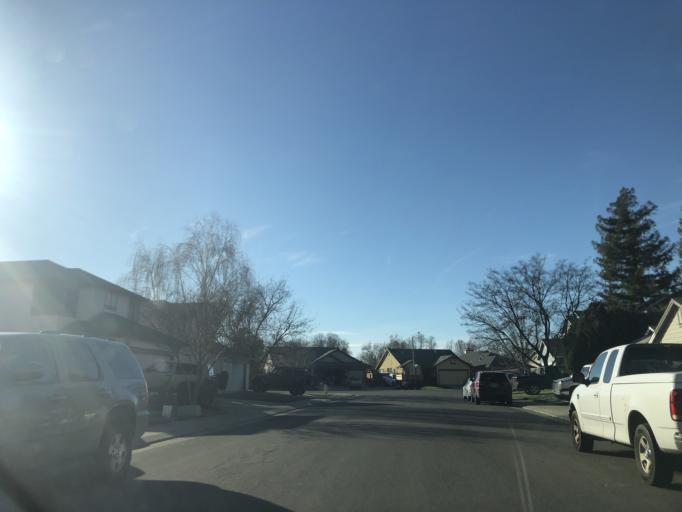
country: US
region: California
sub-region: Yolo County
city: Woodland
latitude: 38.6648
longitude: -121.7490
